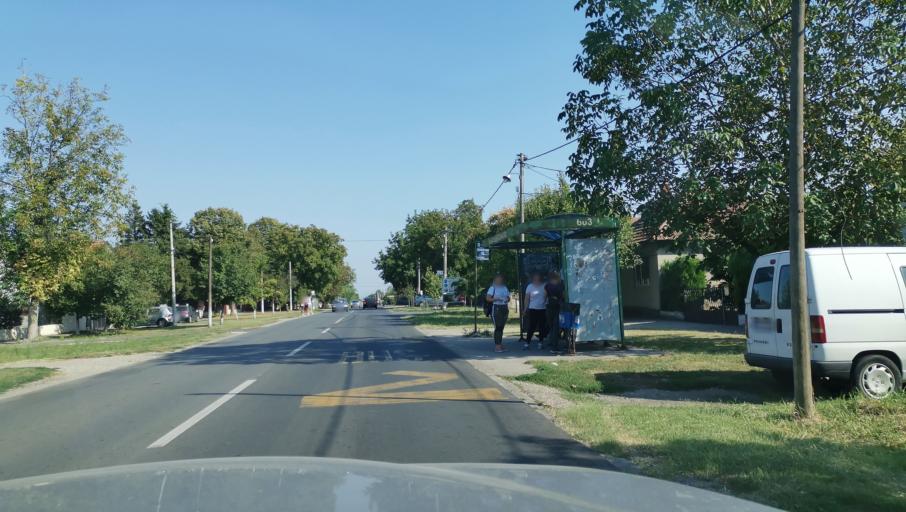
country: RS
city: Dobanovci
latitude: 44.8174
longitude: 20.2331
